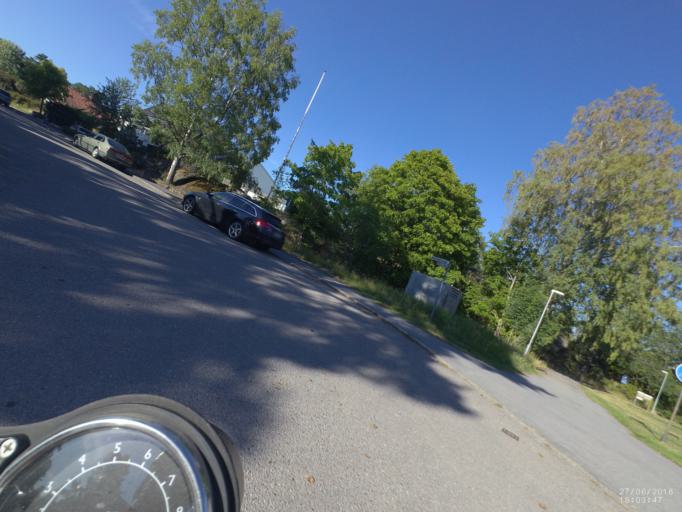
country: SE
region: Soedermanland
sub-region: Nykopings Kommun
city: Nykoping
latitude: 58.7552
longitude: 17.0278
